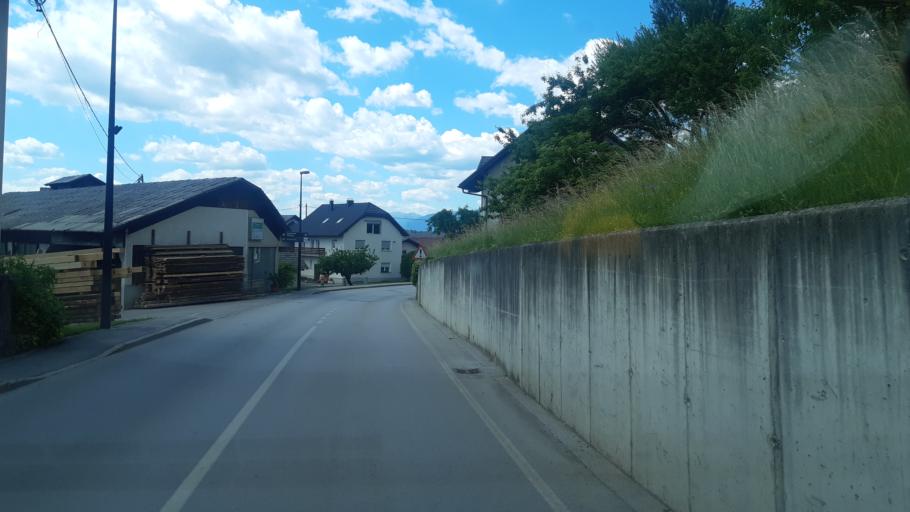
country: SI
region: Vodice
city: Vodice
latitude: 46.1742
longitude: 14.5074
